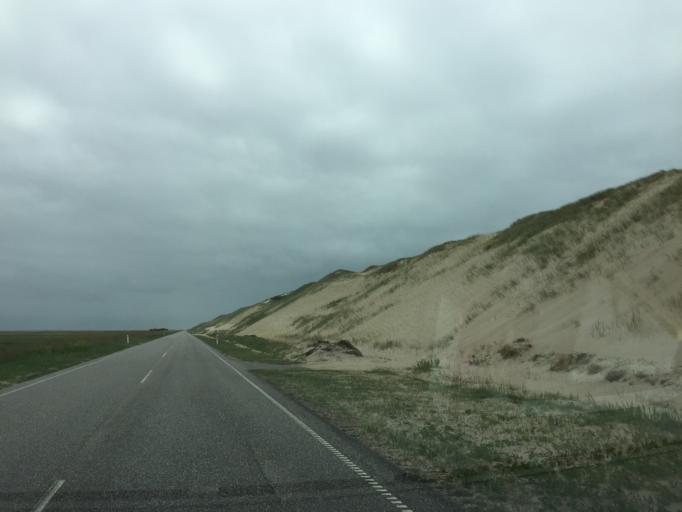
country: DK
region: Central Jutland
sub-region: Lemvig Kommune
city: Harboore
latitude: 56.4447
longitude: 8.1250
